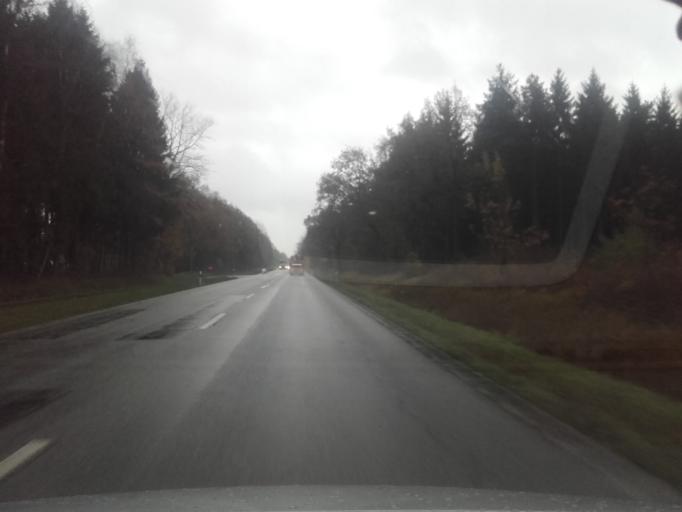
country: DE
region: Schleswig-Holstein
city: Lohe-Fohrden
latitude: 54.3499
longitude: 9.5722
